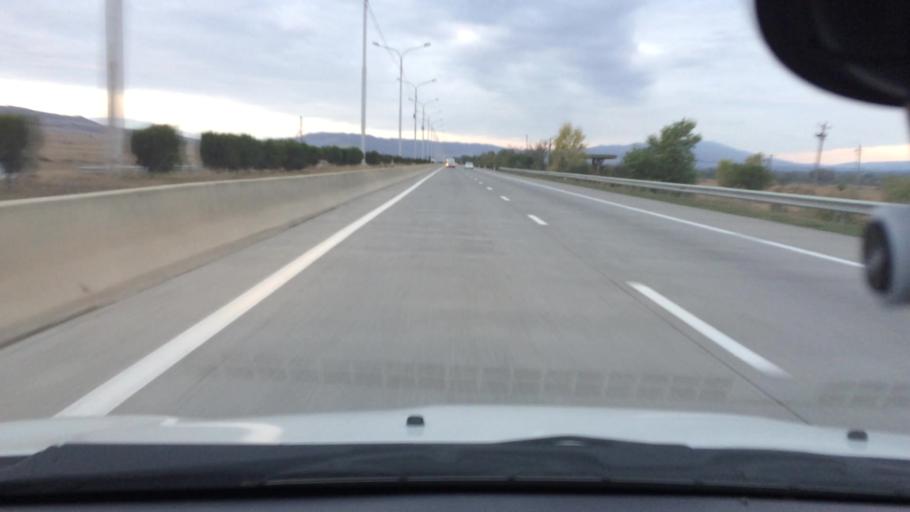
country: GE
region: Mtskheta-Mtianeti
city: Mtskheta
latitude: 41.8950
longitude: 44.6480
